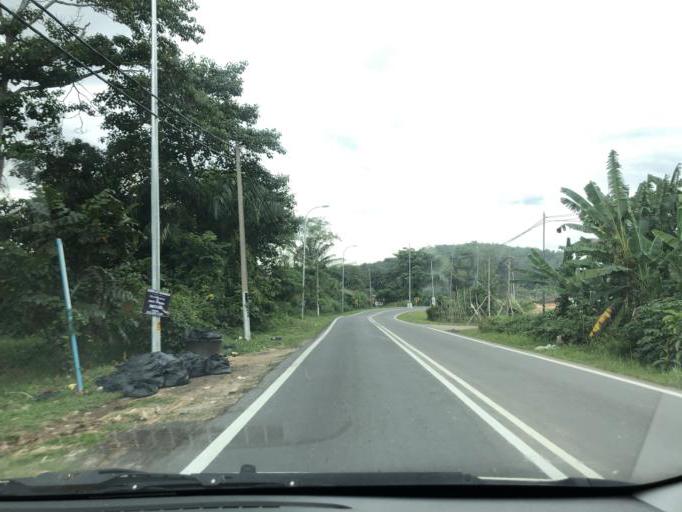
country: MY
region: Putrajaya
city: Putrajaya
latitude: 2.9184
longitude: 101.7516
